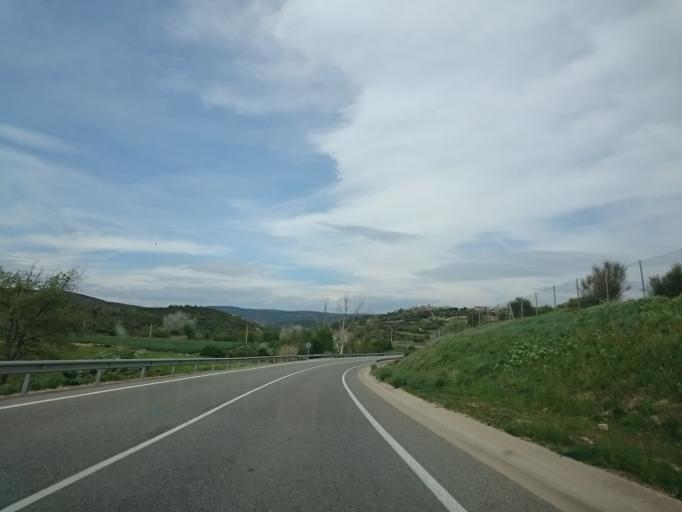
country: ES
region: Catalonia
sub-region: Provincia de Lleida
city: Tora de Riubregos
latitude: 41.8114
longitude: 1.3183
